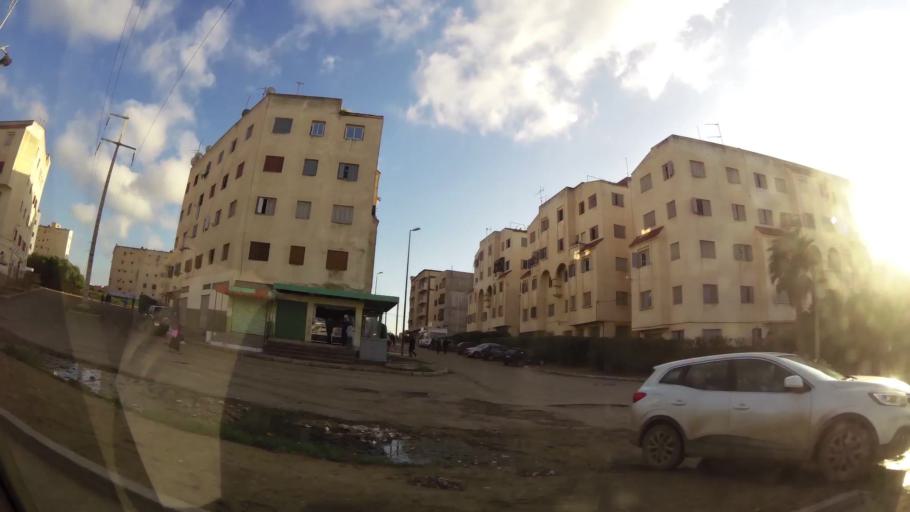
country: MA
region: Chaouia-Ouardigha
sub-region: Settat Province
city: Settat
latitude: 33.0029
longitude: -7.6068
